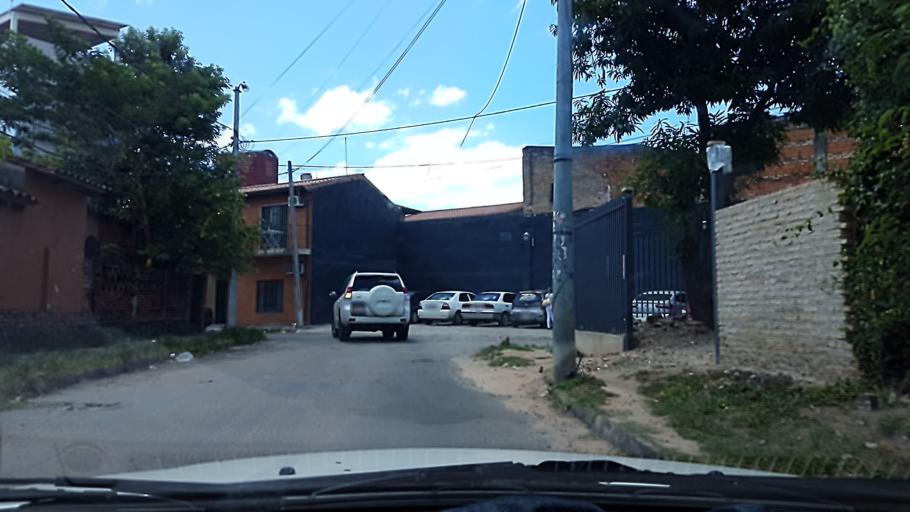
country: PY
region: Asuncion
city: Asuncion
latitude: -25.2757
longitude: -57.6090
